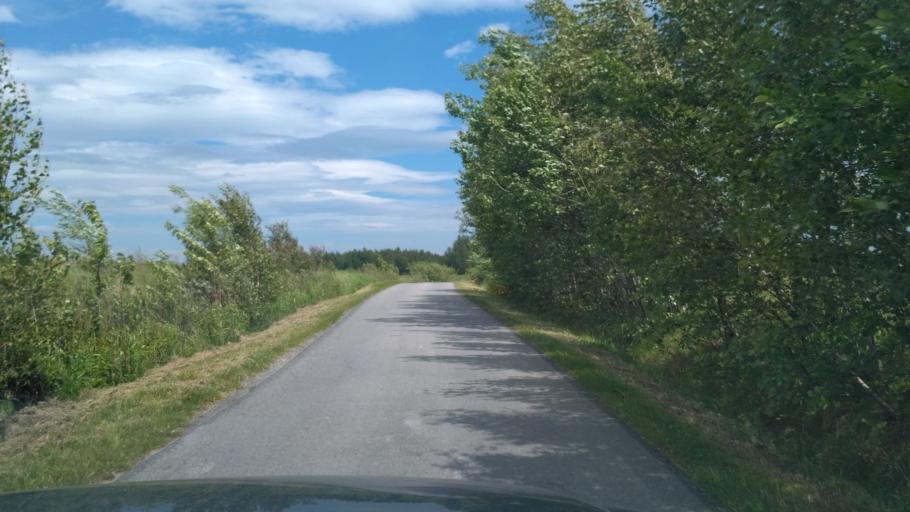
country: PL
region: Subcarpathian Voivodeship
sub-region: Powiat ropczycko-sedziszowski
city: Zagorzyce
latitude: 49.9759
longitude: 21.6570
